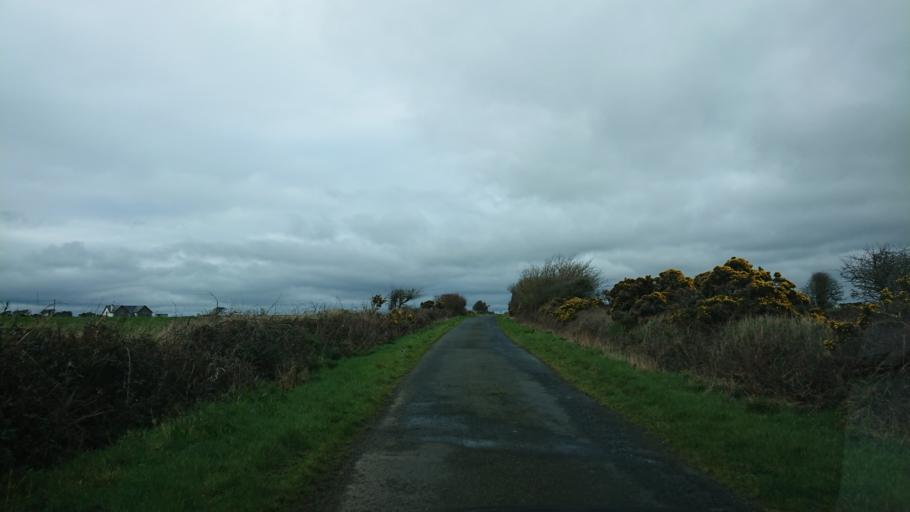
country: IE
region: Munster
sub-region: Waterford
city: Dunmore East
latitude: 52.1500
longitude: -7.0426
